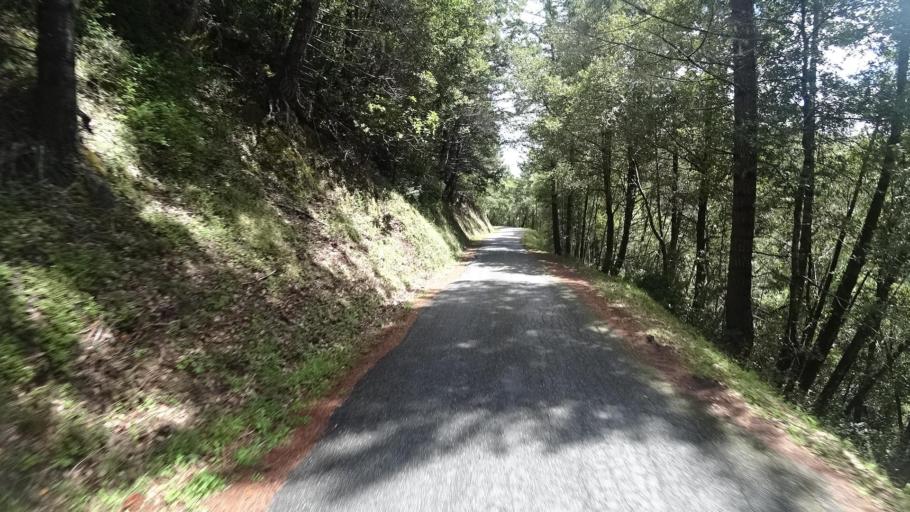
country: US
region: California
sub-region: Humboldt County
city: Blue Lake
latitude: 40.7581
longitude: -123.9150
